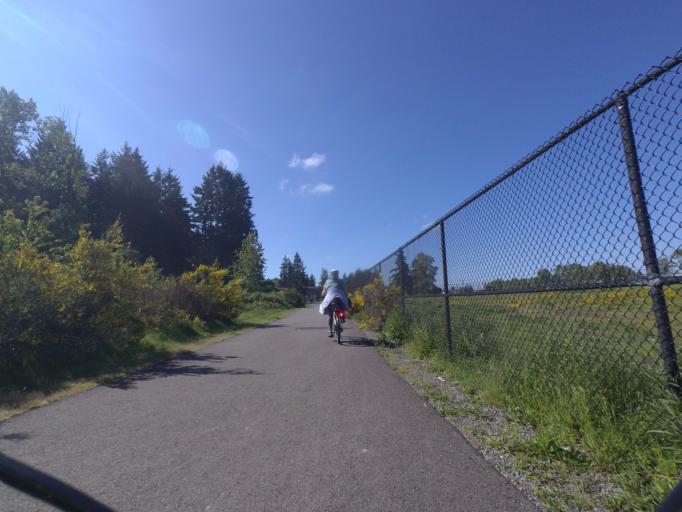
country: US
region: Washington
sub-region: Pierce County
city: Waller
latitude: 47.2081
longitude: -122.4032
